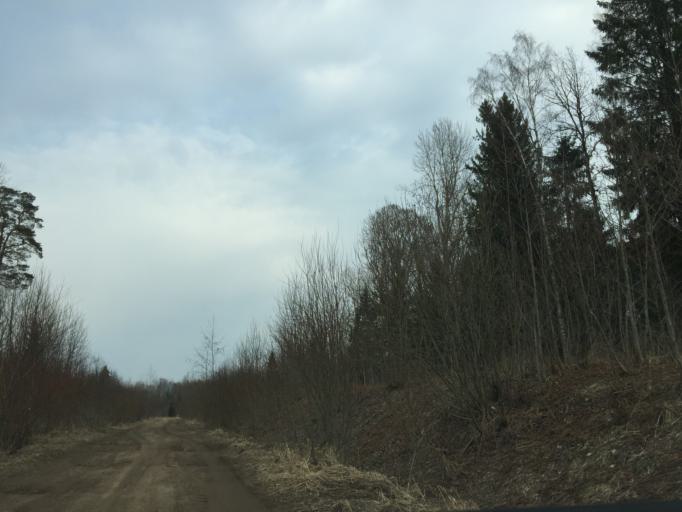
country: LV
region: Priekuli
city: Priekuli
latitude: 57.2063
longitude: 25.3951
